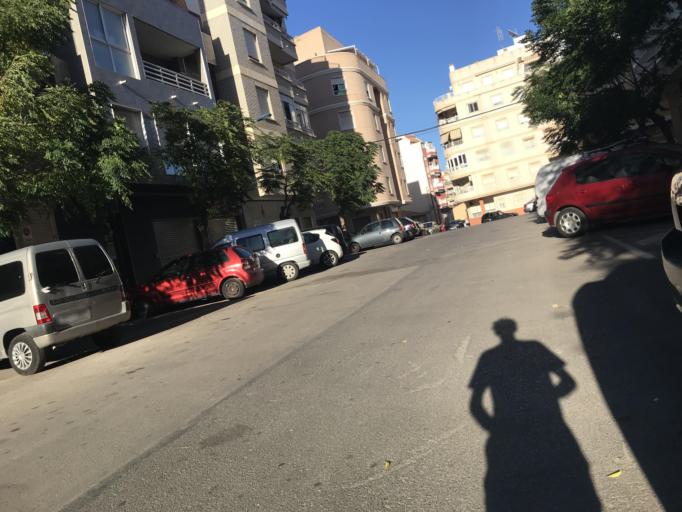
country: ES
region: Valencia
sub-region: Provincia de Alicante
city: Torrevieja
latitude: 37.9812
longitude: -0.6847
